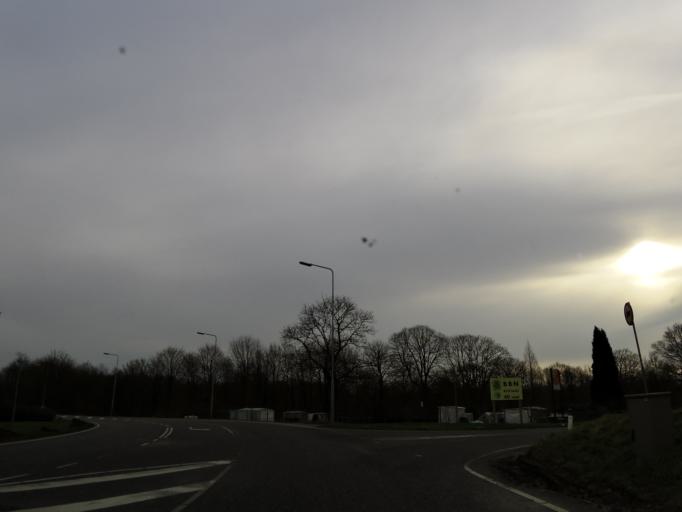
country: NL
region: Limburg
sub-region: Gemeente Nuth
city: Nuth
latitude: 50.9222
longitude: 5.8831
